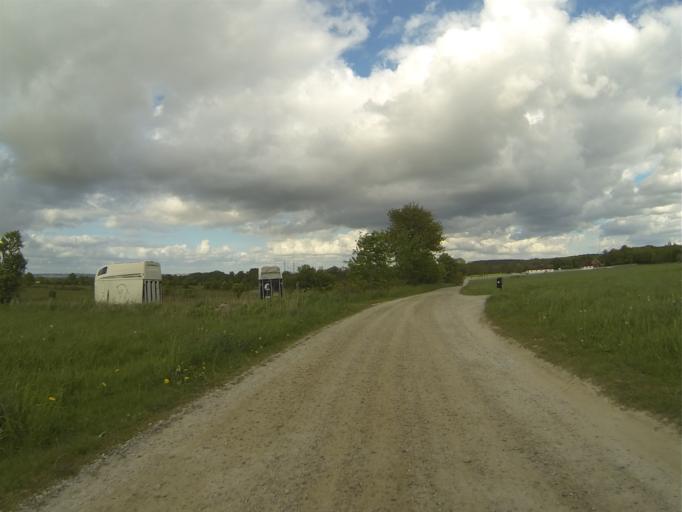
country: SE
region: Skane
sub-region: Lunds Kommun
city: Lund
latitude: 55.7016
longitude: 13.3143
